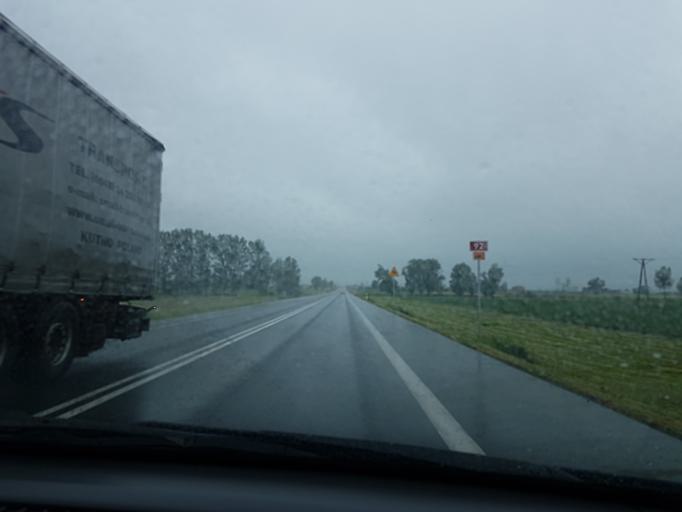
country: PL
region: Greater Poland Voivodeship
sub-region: Powiat kolski
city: Chodow
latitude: 52.2493
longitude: 18.9780
